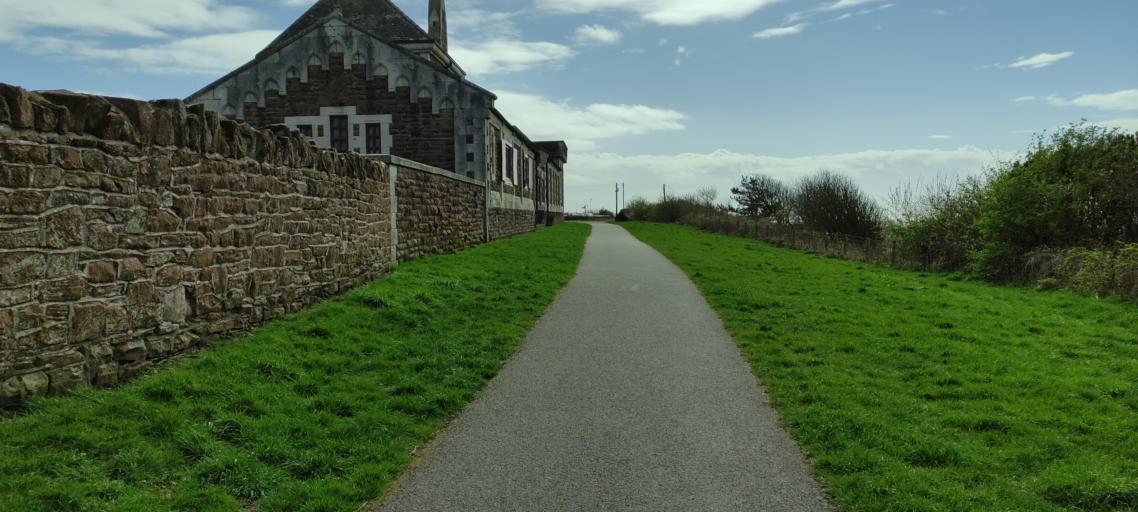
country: GB
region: England
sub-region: Cumbria
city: Maryport
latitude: 54.7216
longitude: -3.4956
